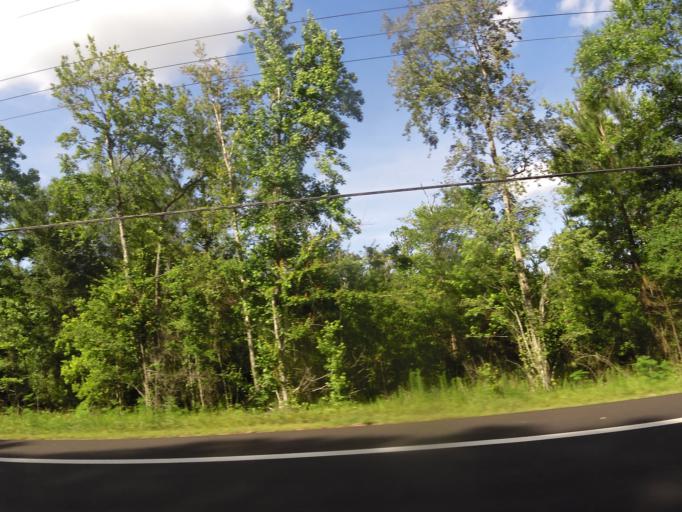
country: US
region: Florida
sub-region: Nassau County
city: Callahan
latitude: 30.5826
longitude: -81.8512
